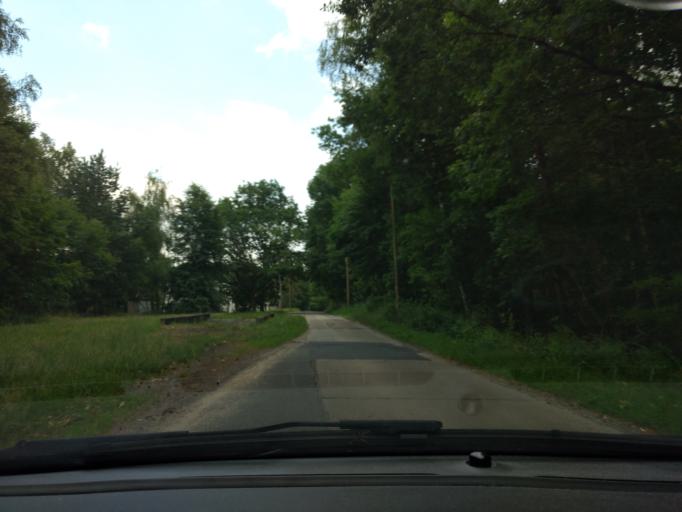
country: DE
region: Saxony
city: Radeburg
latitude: 51.2336
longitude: 13.7288
